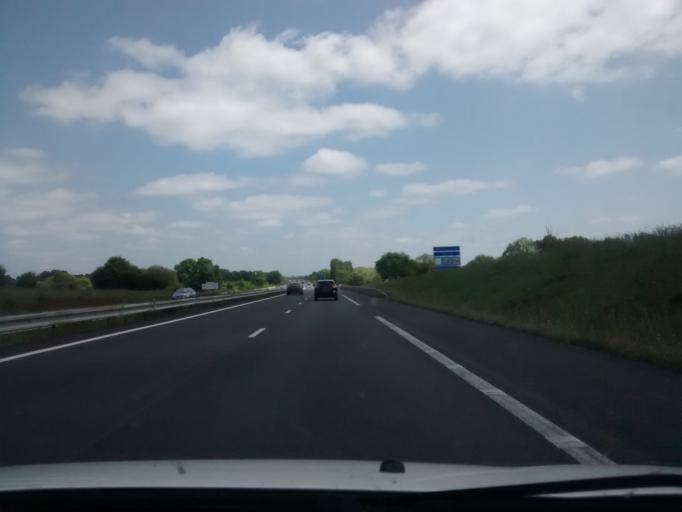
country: FR
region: Pays de la Loire
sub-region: Departement de la Mayenne
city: Vaiges
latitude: 48.0598
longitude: -0.5128
